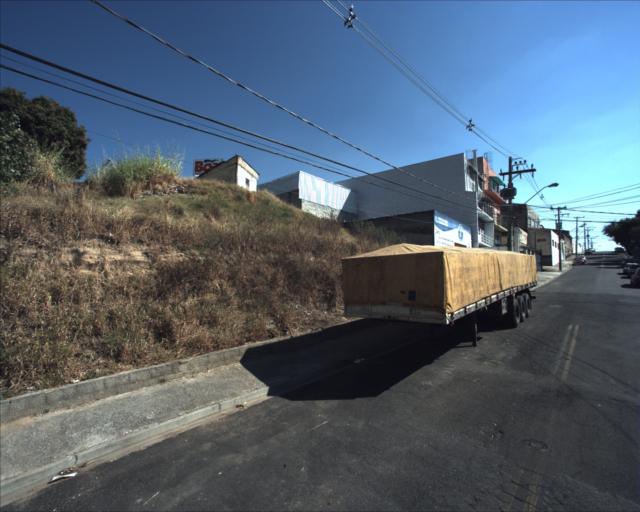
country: BR
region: Sao Paulo
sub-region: Sorocaba
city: Sorocaba
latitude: -23.5115
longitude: -47.4327
